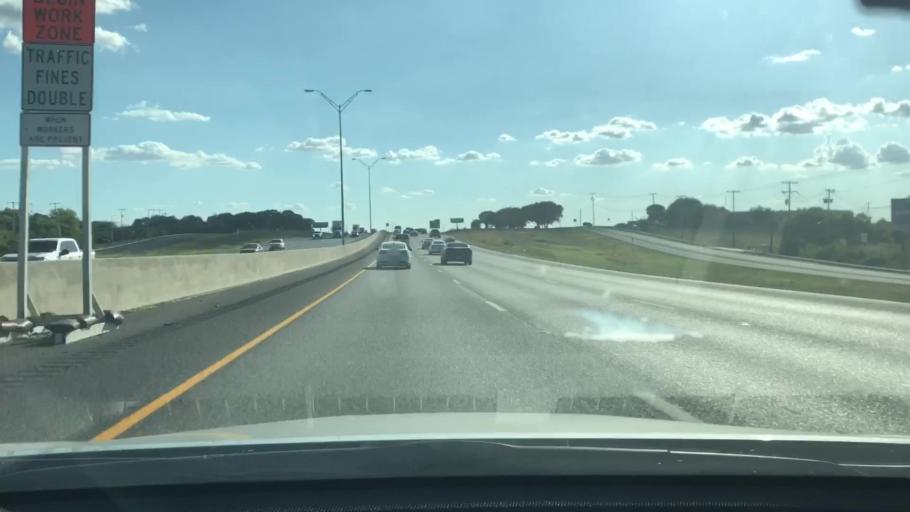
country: US
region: Texas
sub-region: Guadalupe County
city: Northcliff
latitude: 29.6350
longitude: -98.2207
